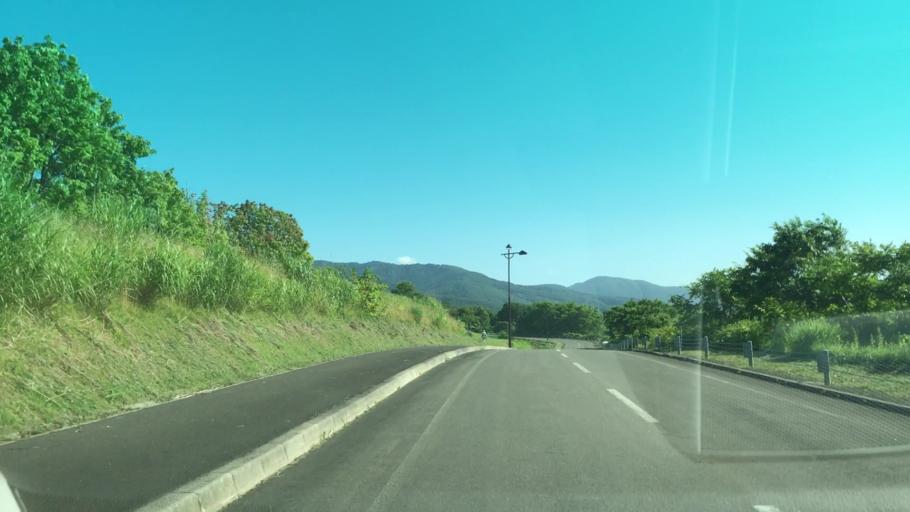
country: JP
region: Hokkaido
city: Iwanai
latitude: 42.9781
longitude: 140.6086
